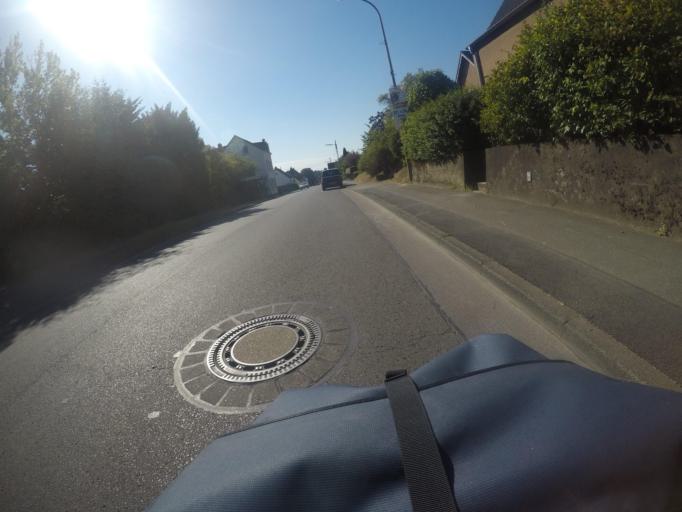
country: DE
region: North Rhine-Westphalia
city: Leichlingen
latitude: 51.0918
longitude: 6.9978
